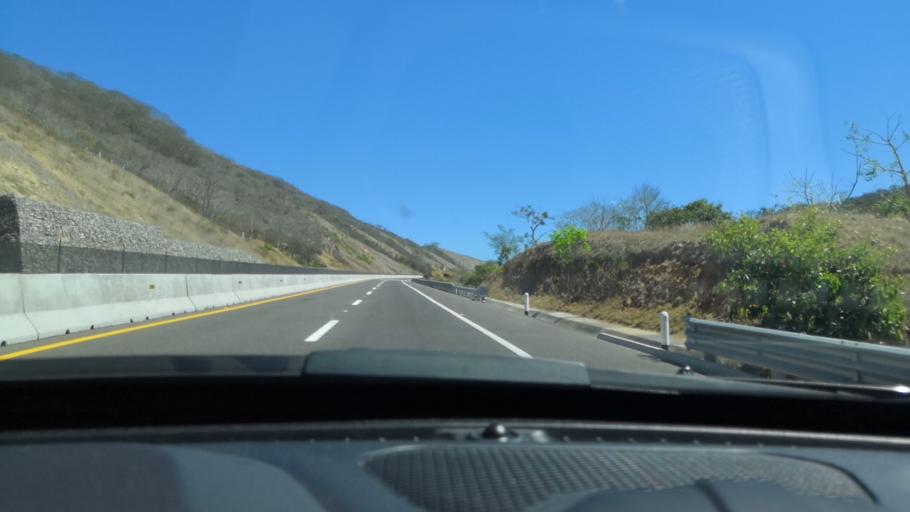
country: MX
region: Nayarit
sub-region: Compostela
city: Juan Escutia (Borbollon)
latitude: 21.1288
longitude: -104.8993
